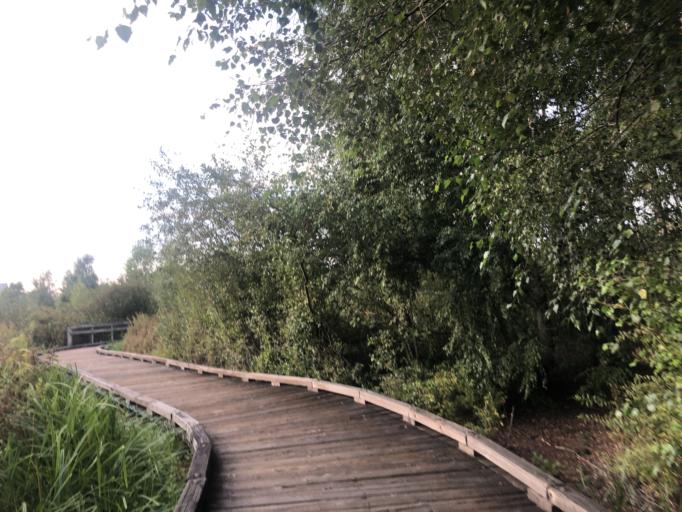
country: US
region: Washington
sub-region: King County
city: Newport
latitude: 47.5887
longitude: -122.1872
